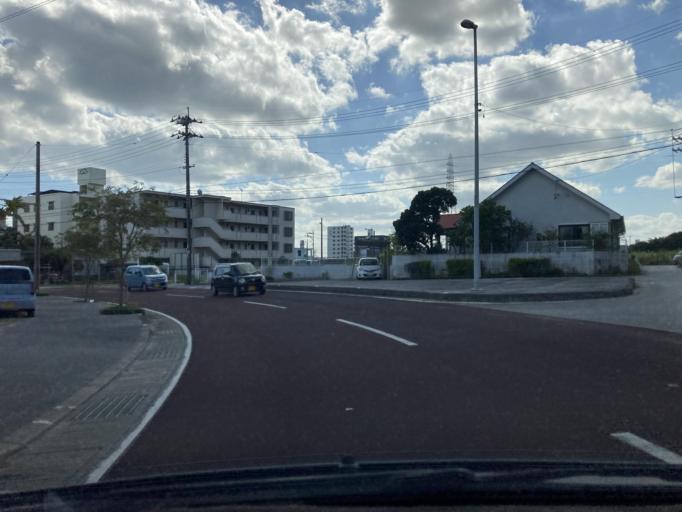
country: JP
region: Okinawa
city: Gushikawa
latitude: 26.3393
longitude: 127.8426
